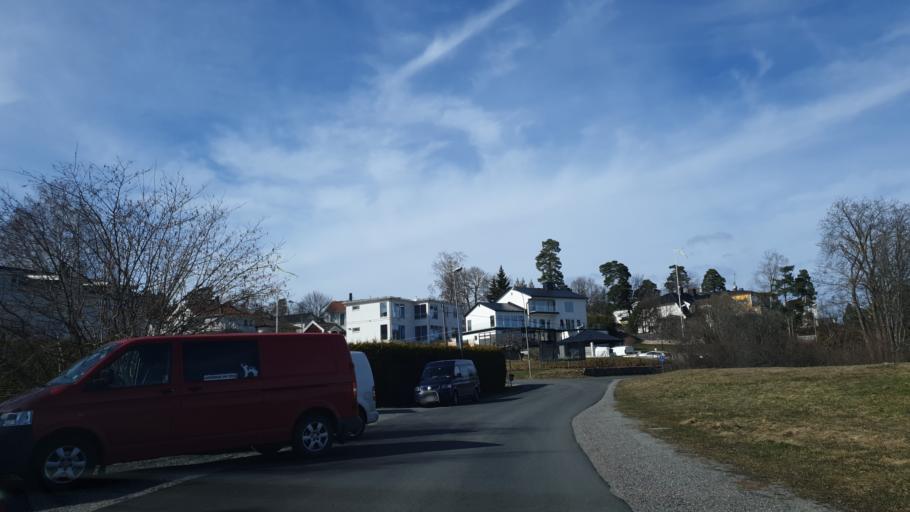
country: SE
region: Stockholm
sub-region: Sollentuna Kommun
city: Sollentuna
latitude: 59.4198
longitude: 17.9824
